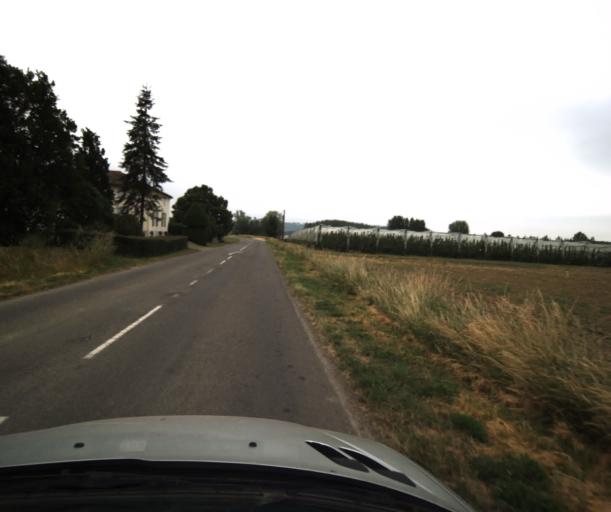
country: FR
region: Midi-Pyrenees
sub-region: Departement du Tarn-et-Garonne
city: Saint-Nicolas-de-la-Grave
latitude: 44.0715
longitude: 1.0247
